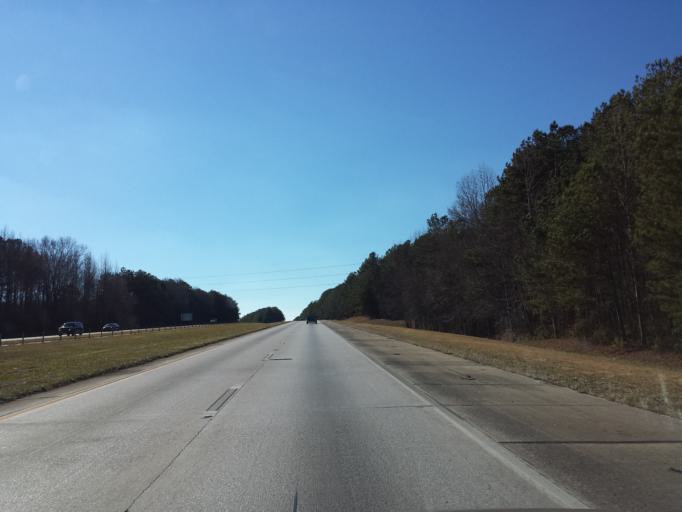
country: US
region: Georgia
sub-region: Carroll County
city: Temple
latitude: 33.7088
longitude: -85.0497
